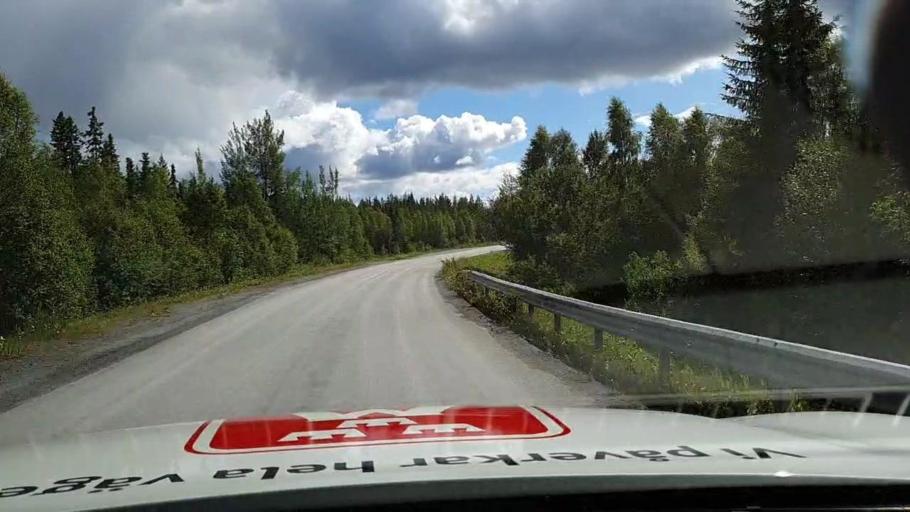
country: SE
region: Jaemtland
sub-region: Krokoms Kommun
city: Valla
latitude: 63.6853
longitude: 13.6832
